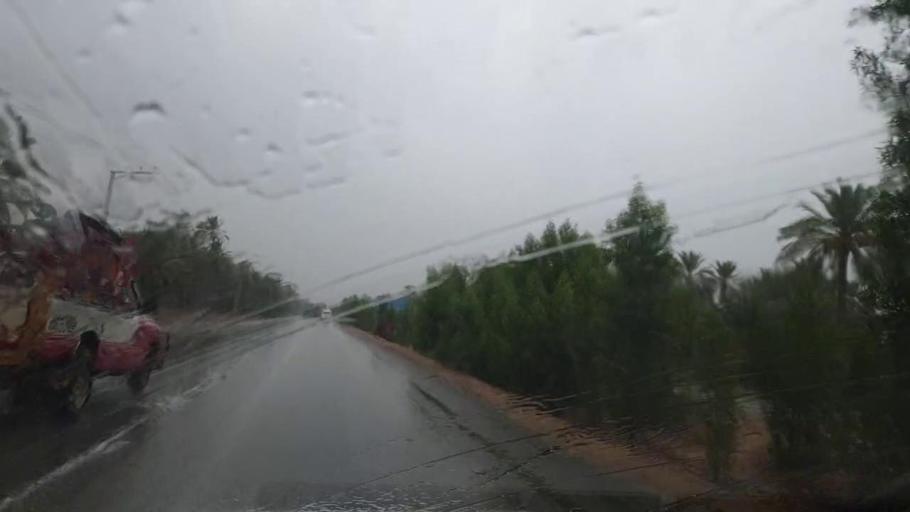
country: PK
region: Sindh
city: Khairpur
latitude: 27.5532
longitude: 68.7343
